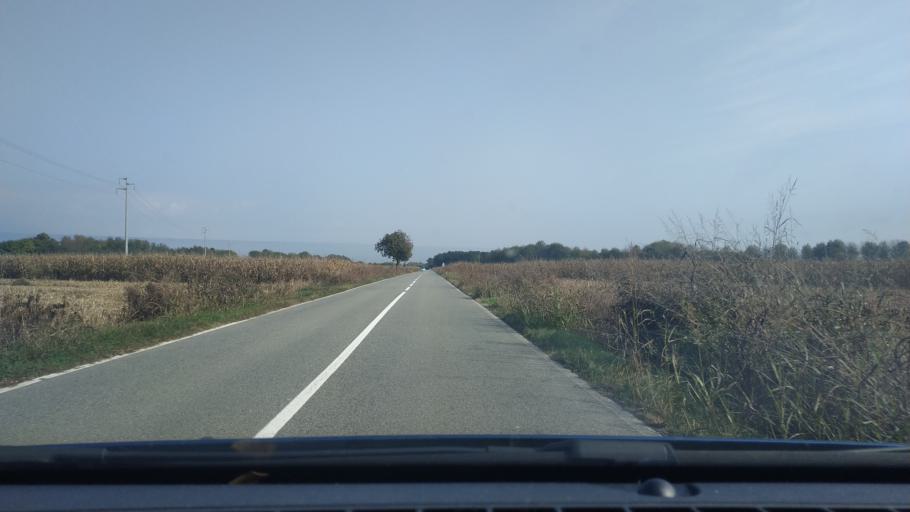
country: IT
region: Piedmont
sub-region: Provincia di Torino
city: Romano Canavese
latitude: 45.4062
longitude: 7.8741
